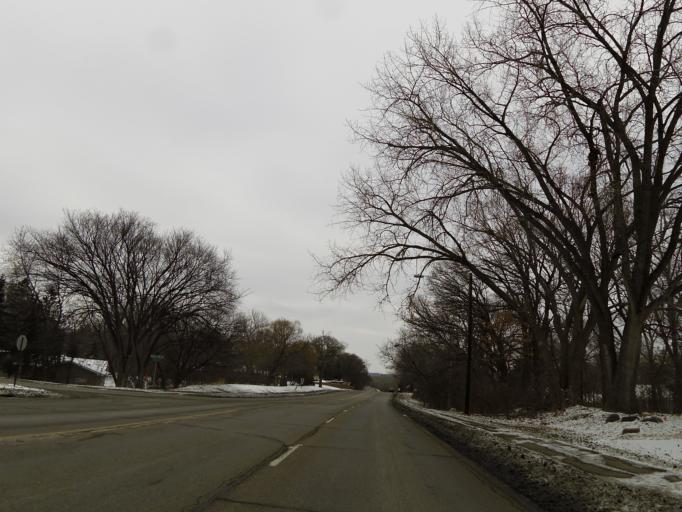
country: US
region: Minnesota
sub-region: Hennepin County
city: Bloomington
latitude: 44.8372
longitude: -93.3502
